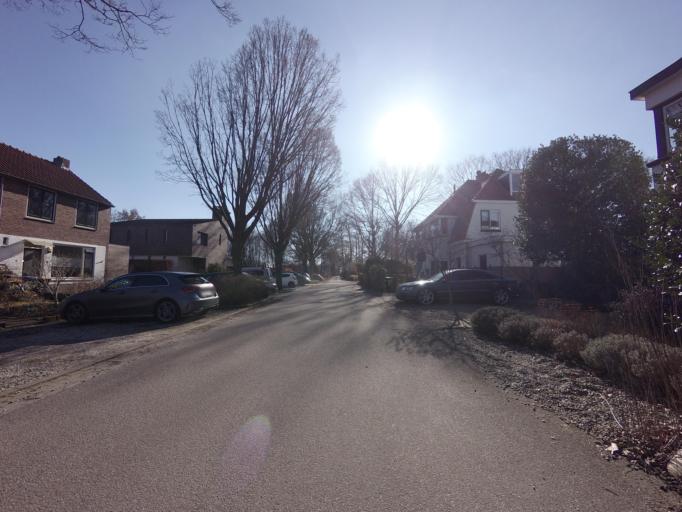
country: NL
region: Utrecht
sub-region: Gemeente De Bilt
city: De Bilt
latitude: 52.1245
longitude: 5.1592
